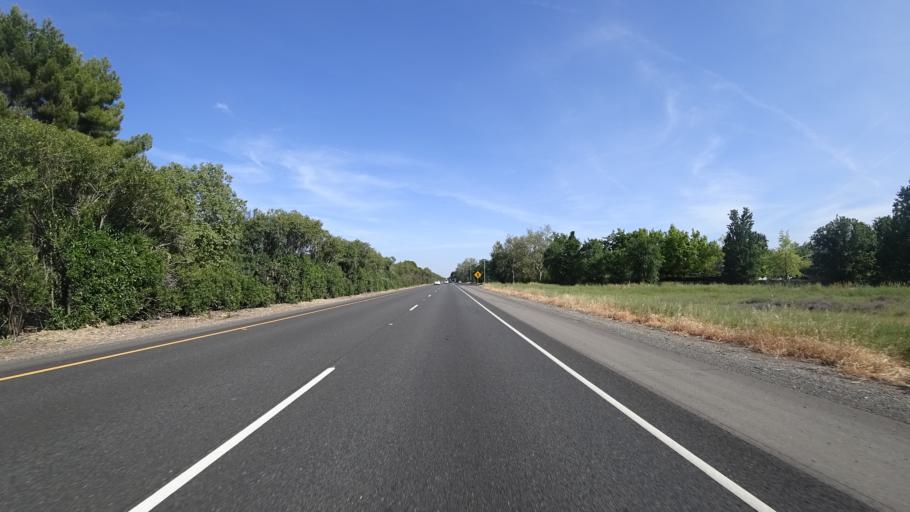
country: US
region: California
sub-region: Butte County
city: Chico
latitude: 39.7737
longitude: -121.8726
